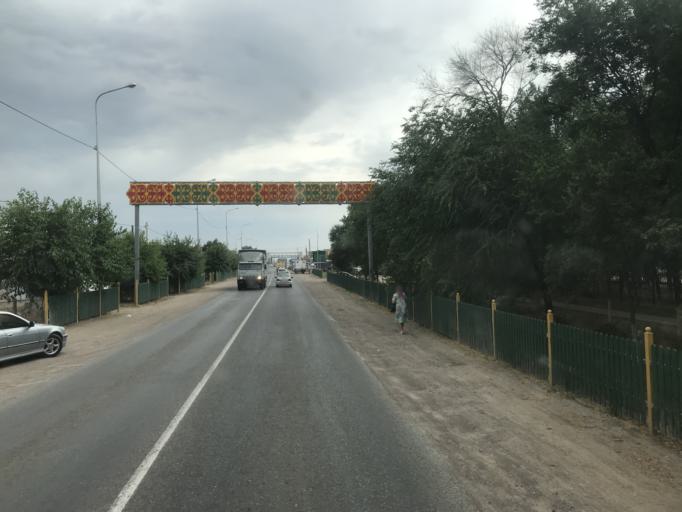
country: KZ
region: Ongtustik Qazaqstan
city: Saryaghash
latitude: 41.3425
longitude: 68.9541
